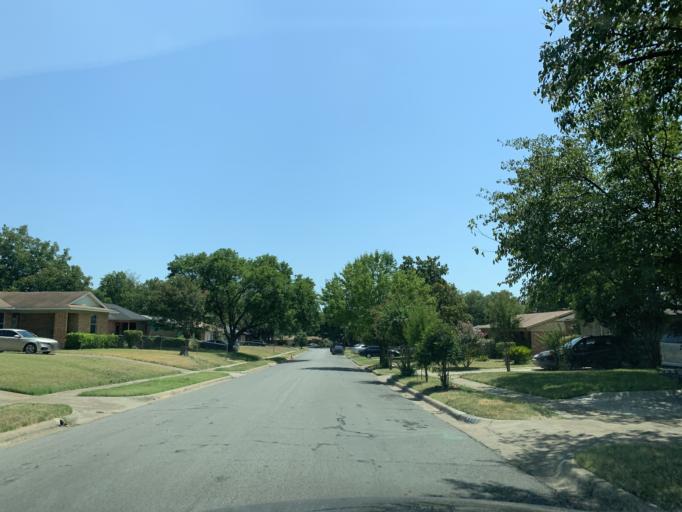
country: US
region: Texas
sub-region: Dallas County
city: Cockrell Hill
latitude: 32.6889
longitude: -96.8075
